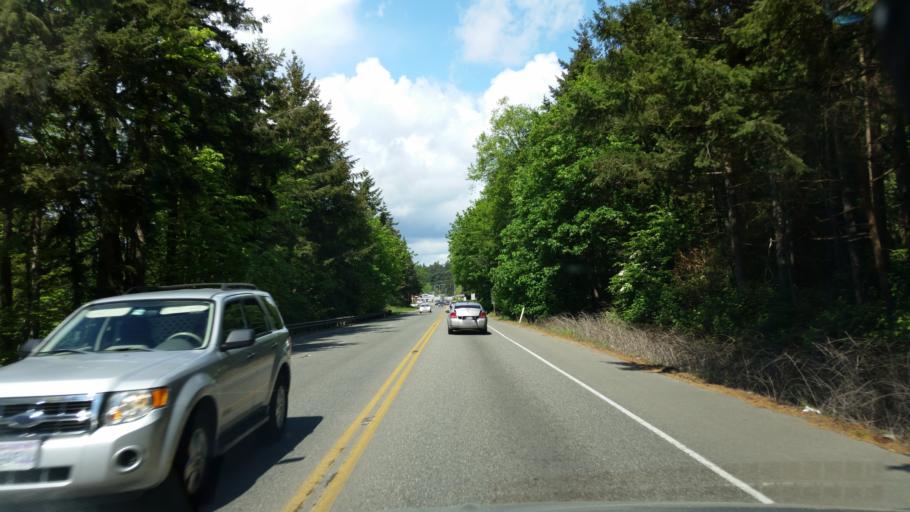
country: US
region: Washington
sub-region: Pierce County
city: Purdy
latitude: 47.3797
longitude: -122.6243
